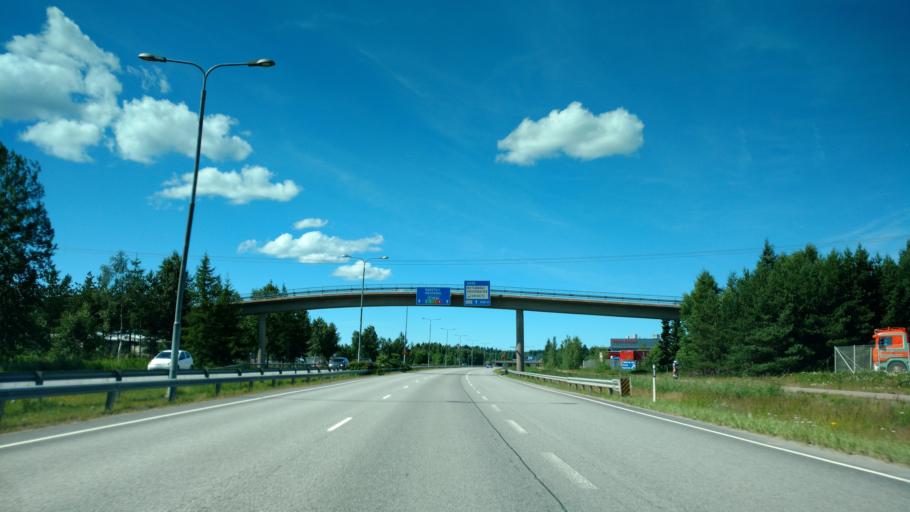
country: FI
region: Varsinais-Suomi
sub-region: Turku
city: Turku
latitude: 60.4823
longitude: 22.3275
